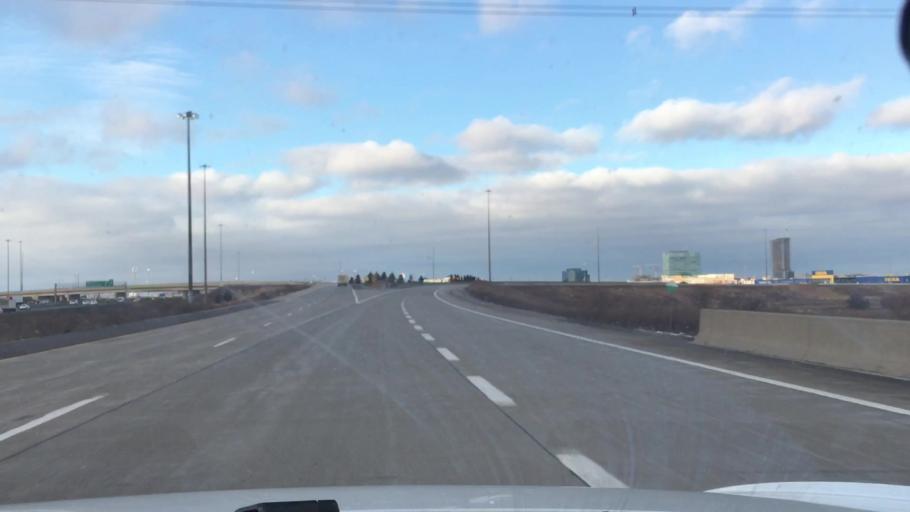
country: CA
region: Ontario
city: Concord
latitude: 43.7780
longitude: -79.5351
